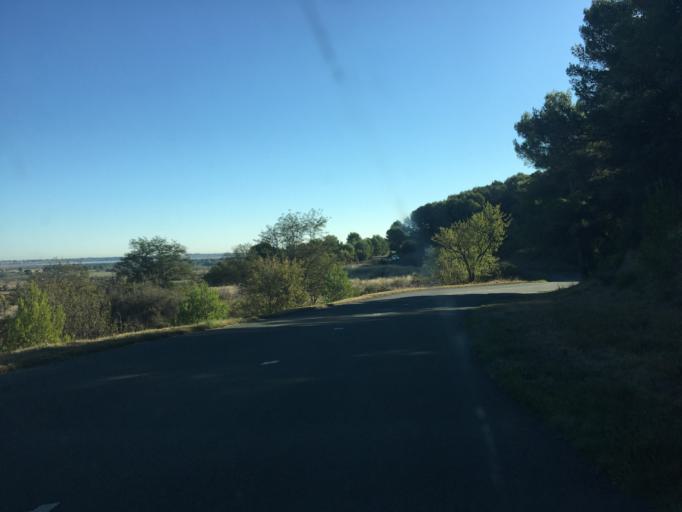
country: FR
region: Languedoc-Roussillon
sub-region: Departement de l'Aude
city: Fleury
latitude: 43.2352
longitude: 3.1709
